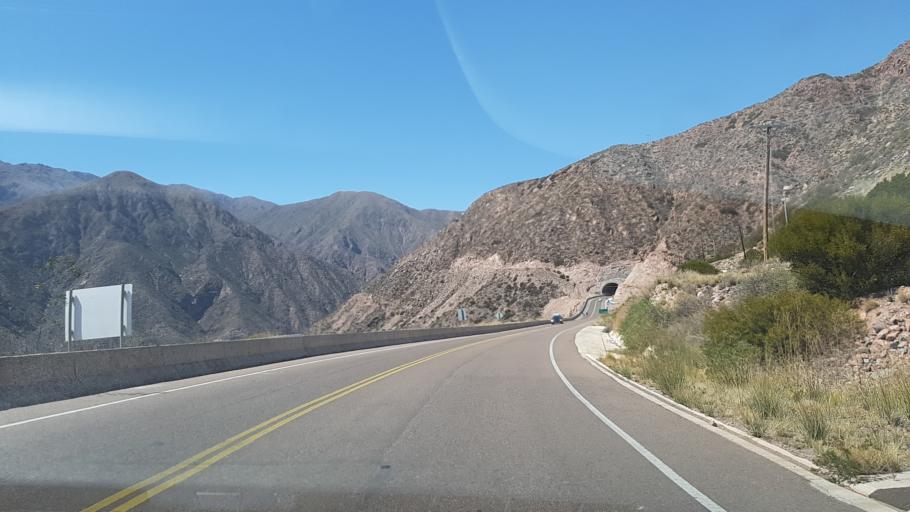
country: AR
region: Mendoza
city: Lujan de Cuyo
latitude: -32.9958
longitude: -69.1424
